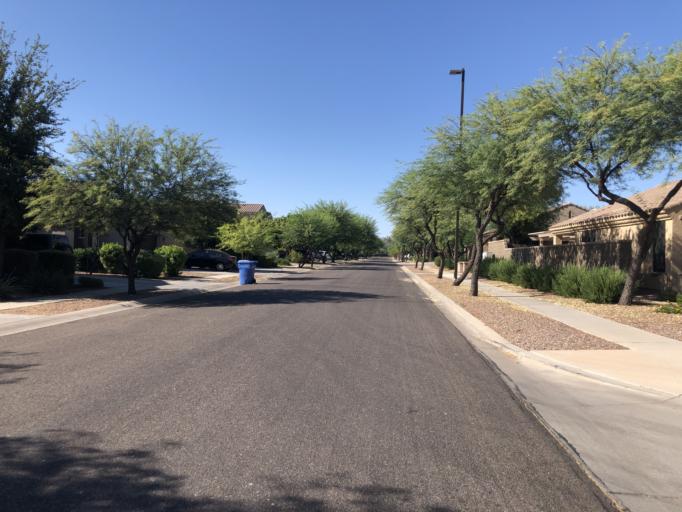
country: US
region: Arizona
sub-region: Maricopa County
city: Queen Creek
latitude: 33.2814
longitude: -111.6919
